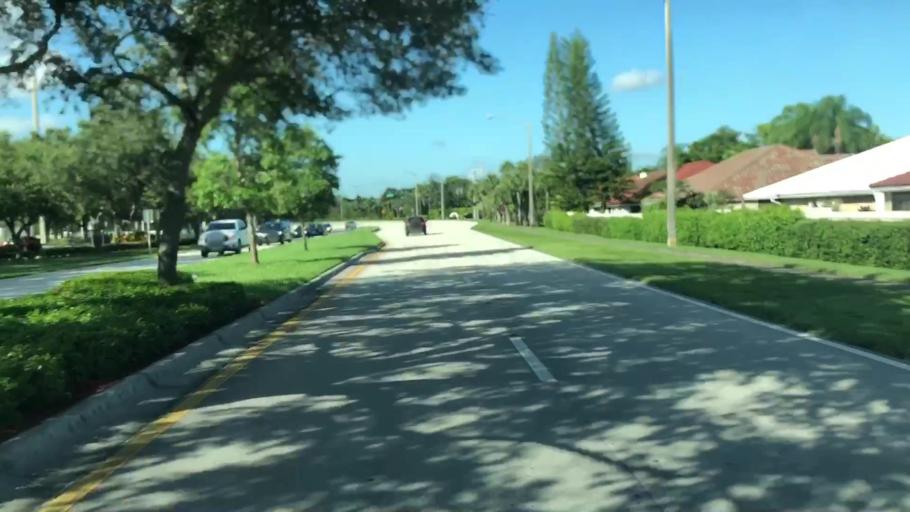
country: US
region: Florida
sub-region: Broward County
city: Coral Springs
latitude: 26.2504
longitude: -80.2673
